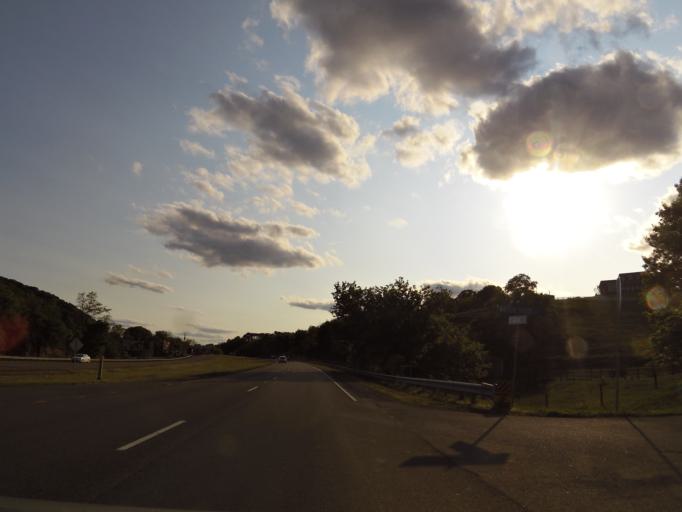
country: US
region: Virginia
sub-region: Russell County
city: Honaker
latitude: 36.9569
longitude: -81.9385
